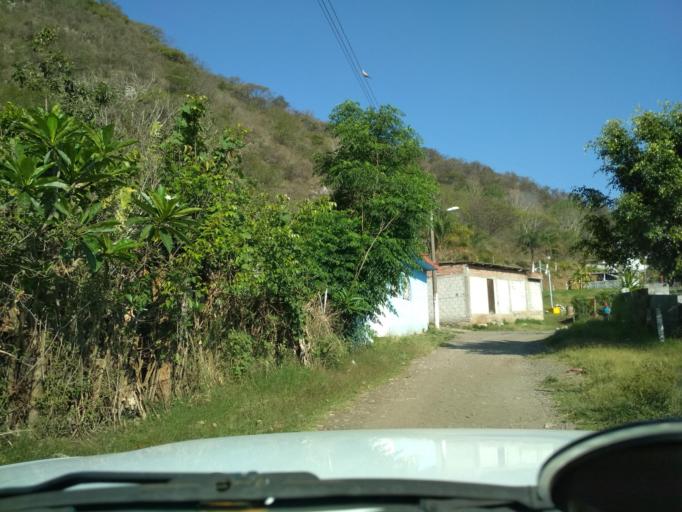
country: MX
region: Veracruz
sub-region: Nogales
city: Agricola Lazaro Cardenas
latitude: 18.8056
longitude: -97.2004
